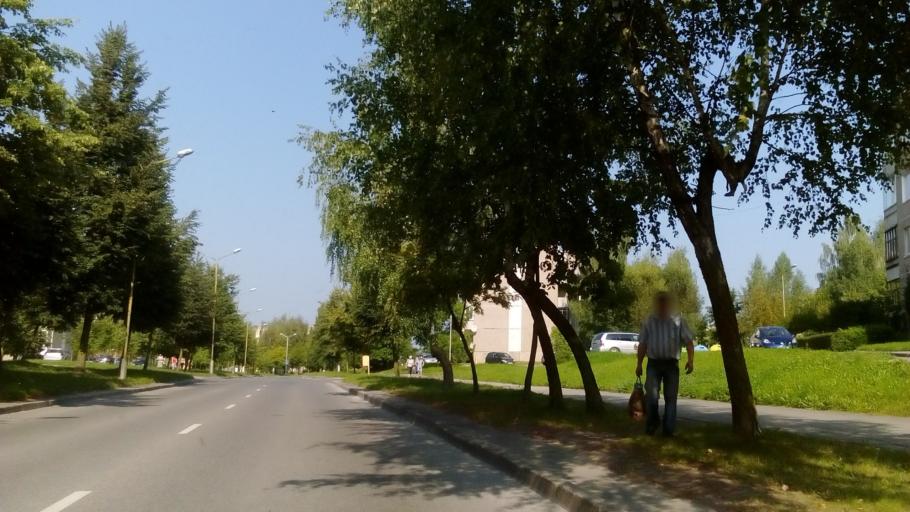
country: LT
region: Alytaus apskritis
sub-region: Alytus
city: Alytus
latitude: 54.3965
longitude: 24.0201
